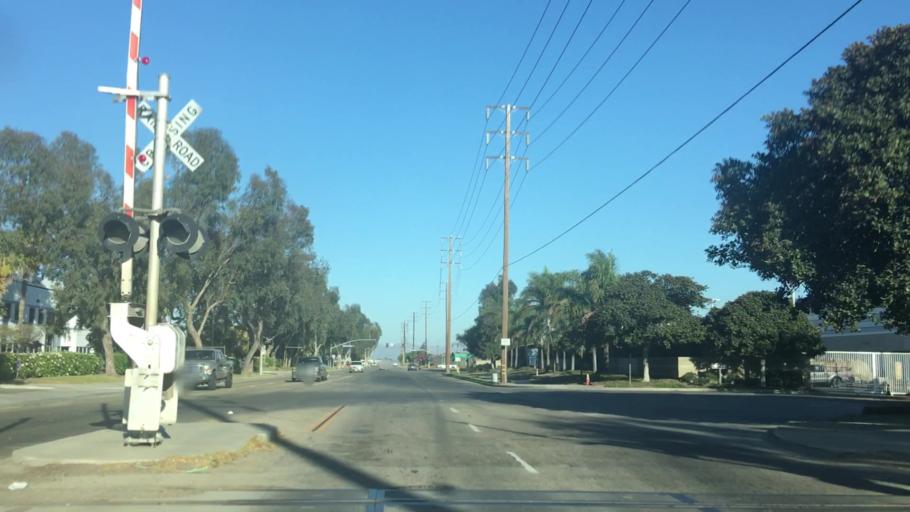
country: US
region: California
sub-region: Ventura County
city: Oxnard
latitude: 34.2019
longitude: -119.1299
